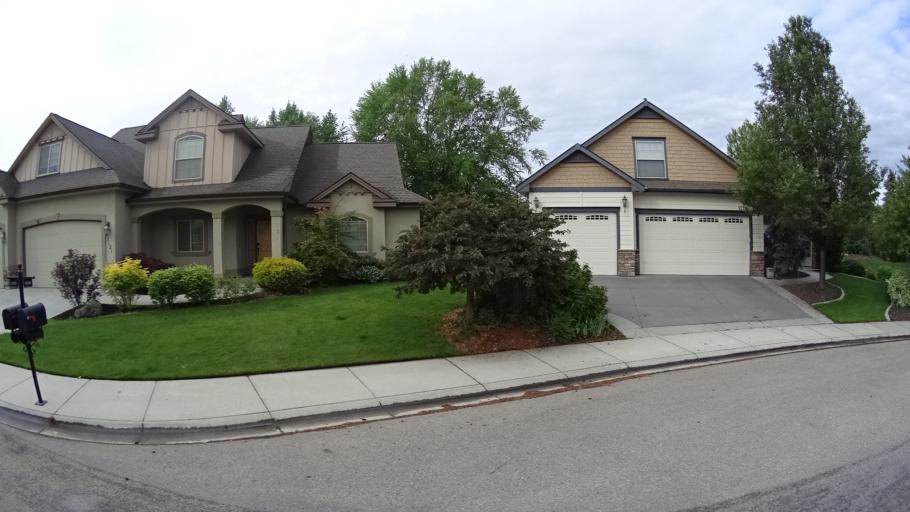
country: US
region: Idaho
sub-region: Ada County
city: Star
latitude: 43.6887
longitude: -116.5048
